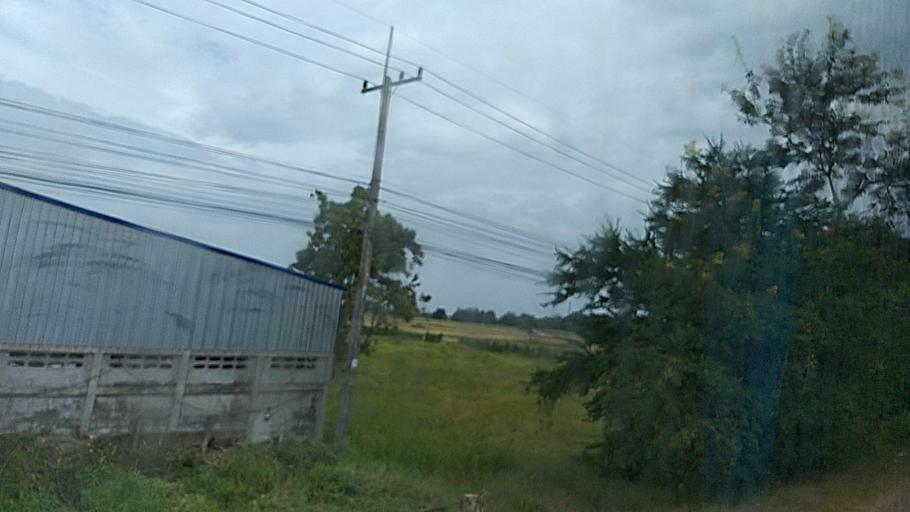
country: TH
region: Maha Sarakham
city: Maha Sarakham
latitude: 16.1512
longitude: 103.3831
